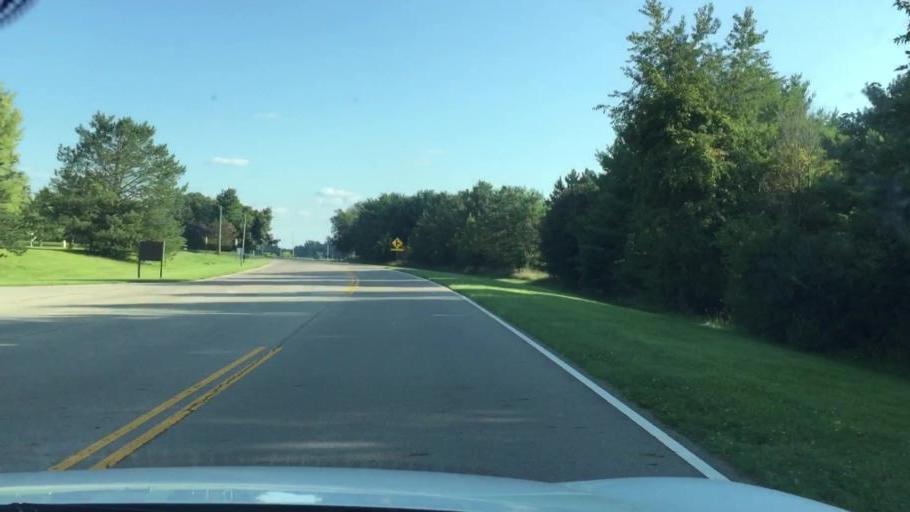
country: US
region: Ohio
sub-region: Clark County
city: Northridge
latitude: 39.9479
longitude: -83.7298
